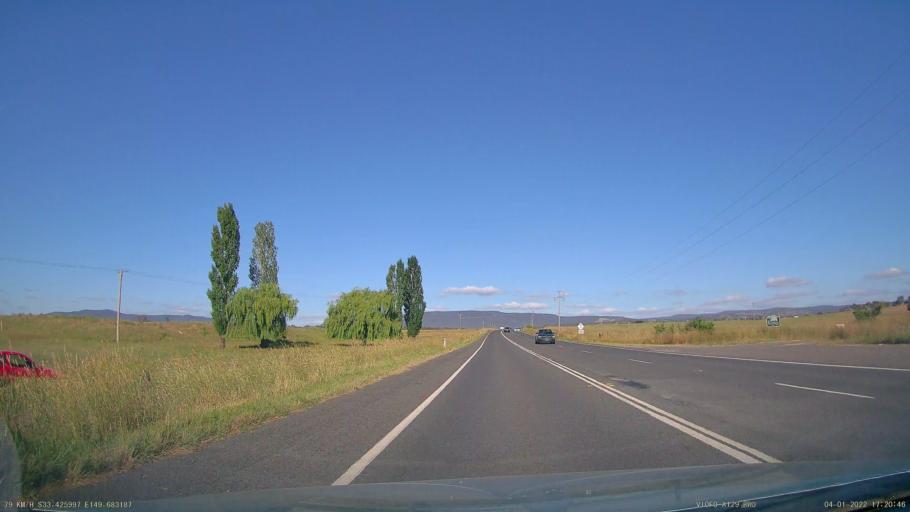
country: AU
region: New South Wales
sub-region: Bathurst Regional
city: Kelso
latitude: -33.4260
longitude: 149.6834
